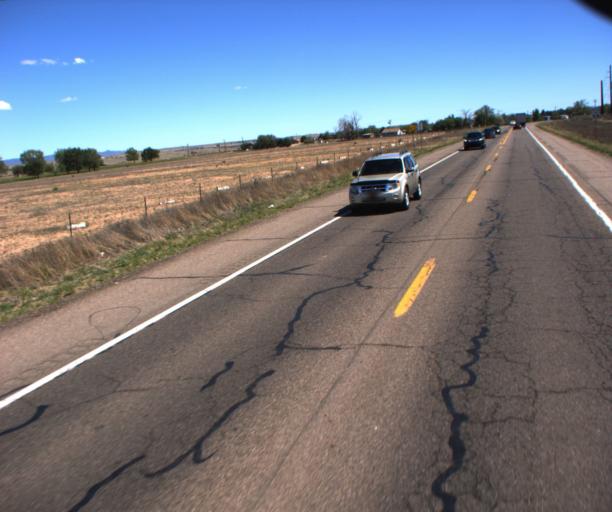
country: US
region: Arizona
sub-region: Yavapai County
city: Chino Valley
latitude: 34.8079
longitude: -112.4512
